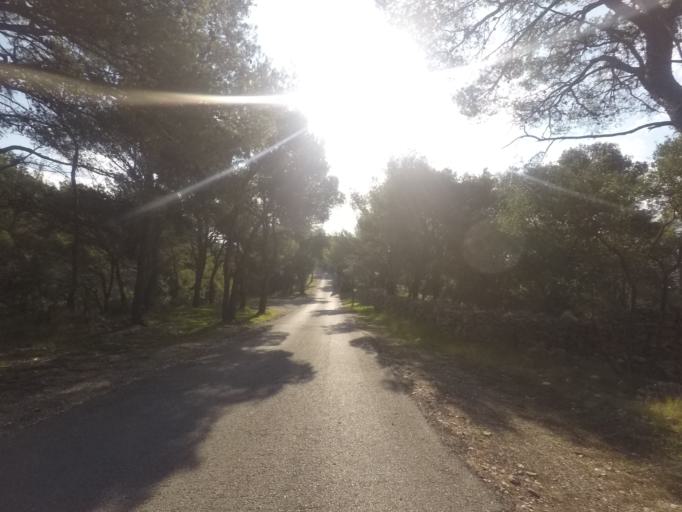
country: HR
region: Splitsko-Dalmatinska
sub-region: Grad Hvar
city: Hvar
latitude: 43.1756
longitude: 16.4398
